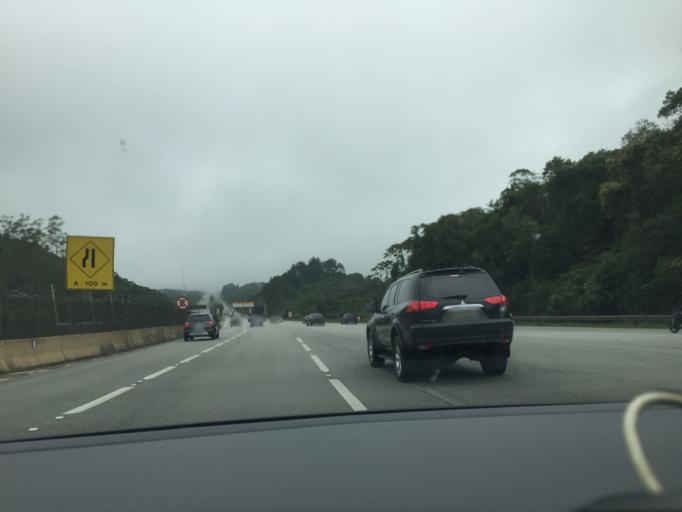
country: BR
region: Sao Paulo
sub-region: Sao Bernardo Do Campo
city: Sao Bernardo do Campo
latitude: -23.8239
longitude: -46.5818
